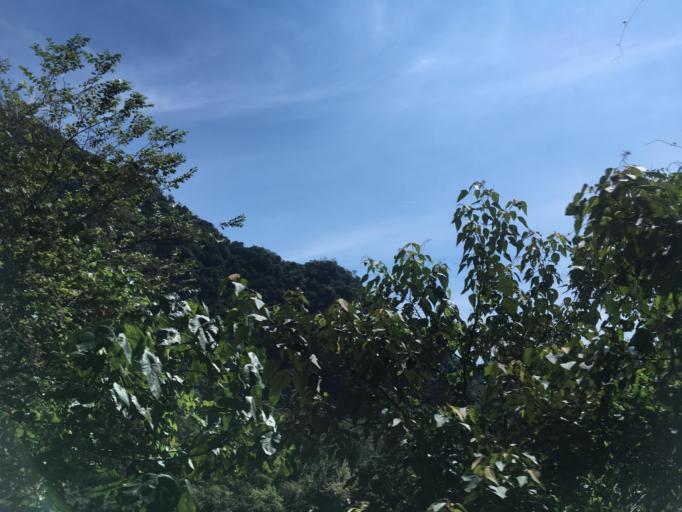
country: TW
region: Taiwan
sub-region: Yilan
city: Yilan
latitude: 24.4211
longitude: 121.7277
